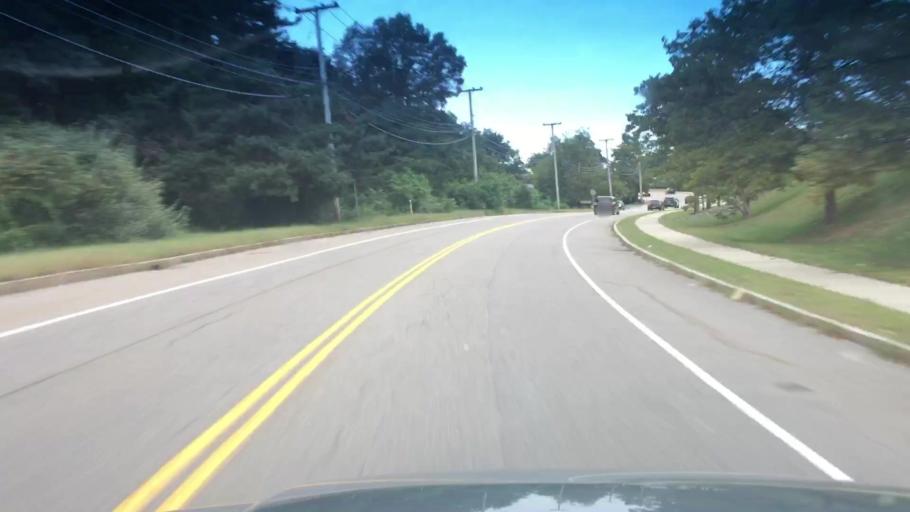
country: US
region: Massachusetts
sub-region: Norfolk County
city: Norwood
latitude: 42.2055
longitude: -71.1806
